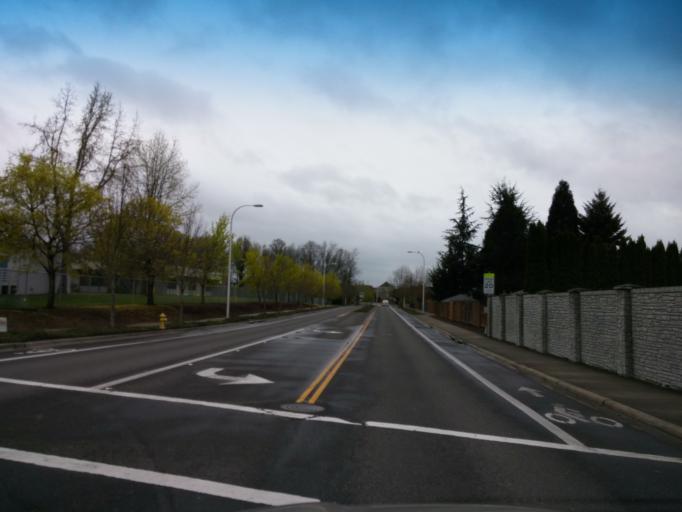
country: US
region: Oregon
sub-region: Washington County
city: Aloha
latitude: 45.5164
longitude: -122.8527
